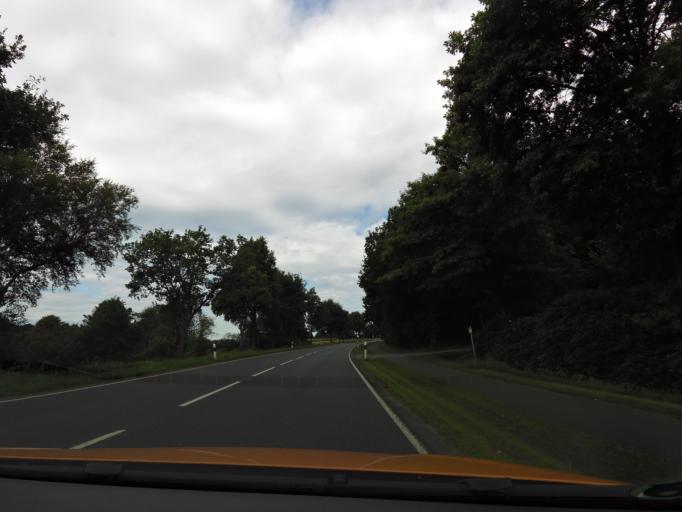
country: DE
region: Lower Saxony
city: Wiefelstede
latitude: 53.1707
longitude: 8.1344
